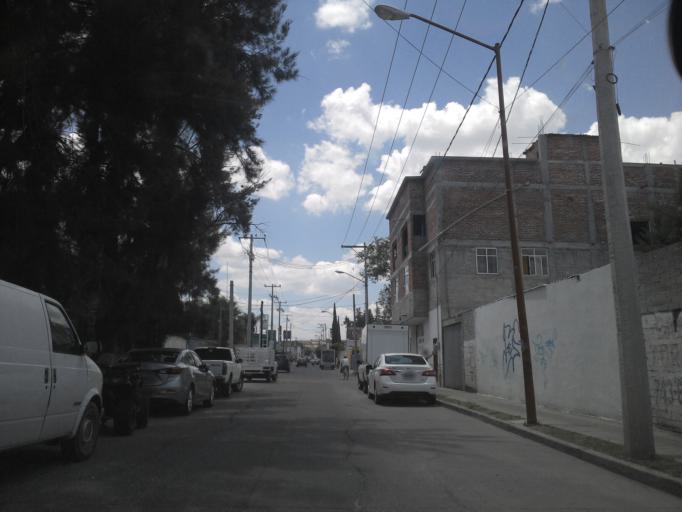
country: MX
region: Guanajuato
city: San Francisco del Rincon
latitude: 21.0258
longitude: -101.8575
